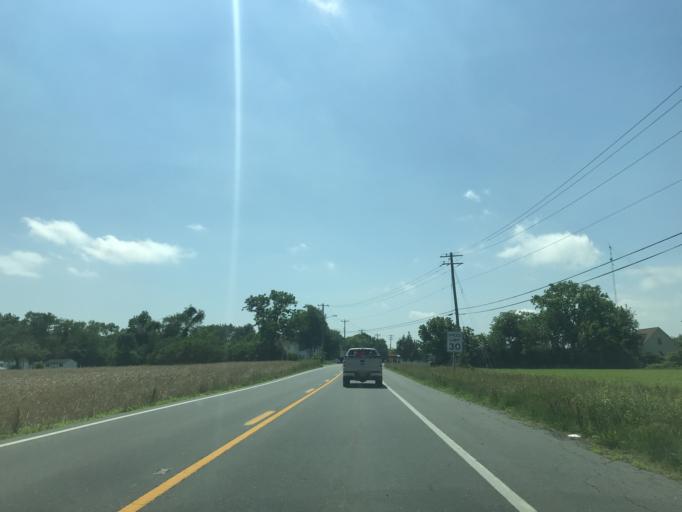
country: US
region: Maryland
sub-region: Dorchester County
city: Hurlock
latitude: 38.5970
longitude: -75.9122
